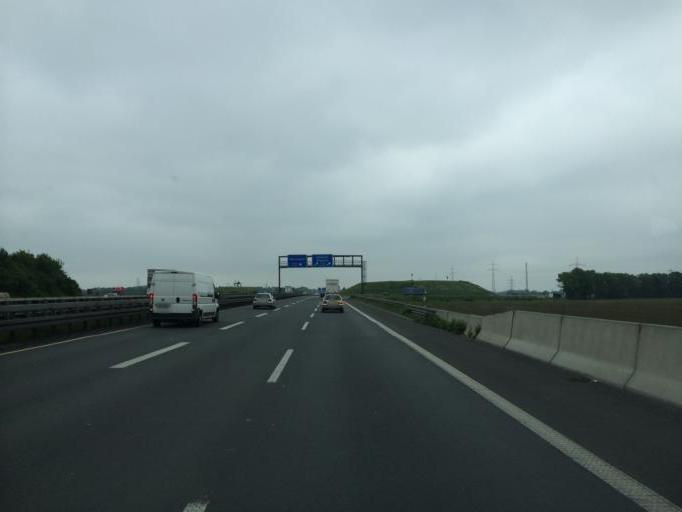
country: DE
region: North Rhine-Westphalia
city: Kamen
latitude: 51.5963
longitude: 7.6865
